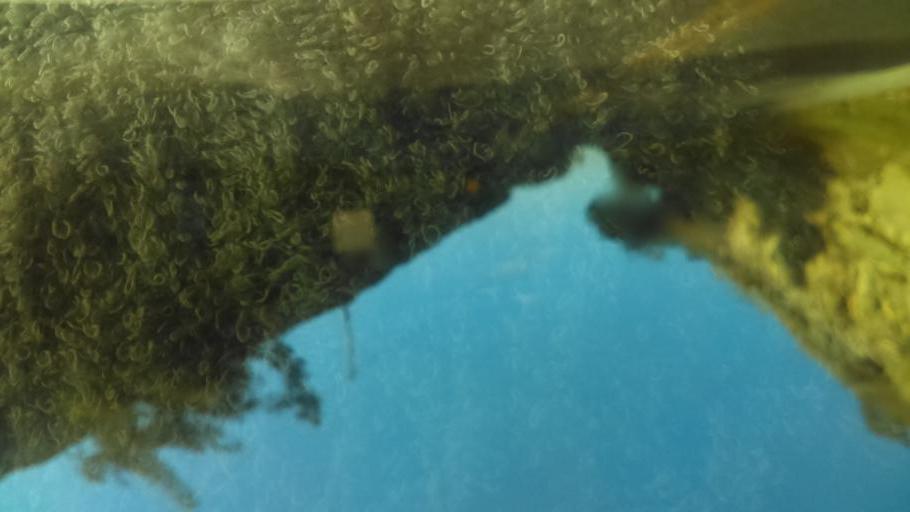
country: CO
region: Cundinamarca
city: Mosquera
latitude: 4.6605
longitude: -74.2852
